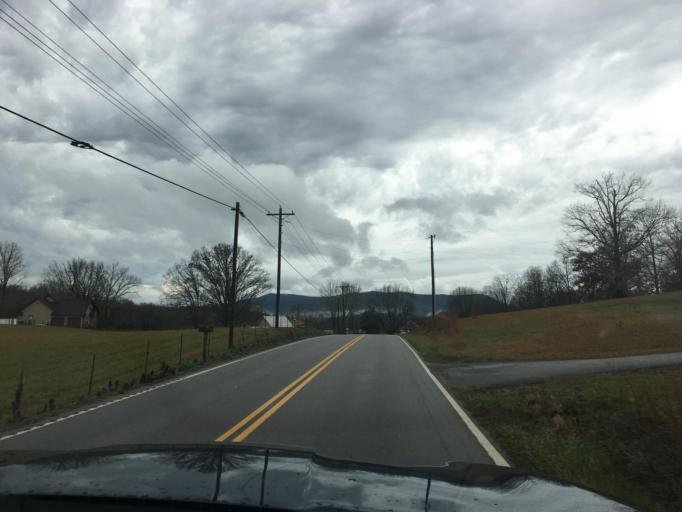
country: US
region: Tennessee
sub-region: Monroe County
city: Madisonville
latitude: 35.3583
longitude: -84.3357
